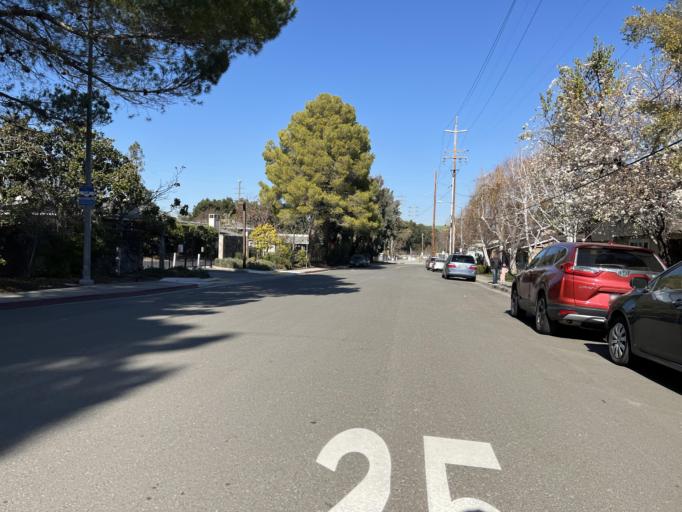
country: US
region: California
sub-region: Santa Clara County
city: Loyola
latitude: 37.3224
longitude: -122.0740
